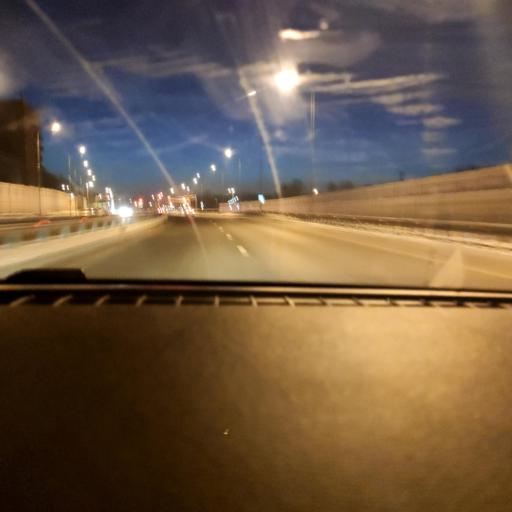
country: RU
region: Samara
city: Bereza
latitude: 53.5123
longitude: 50.1469
